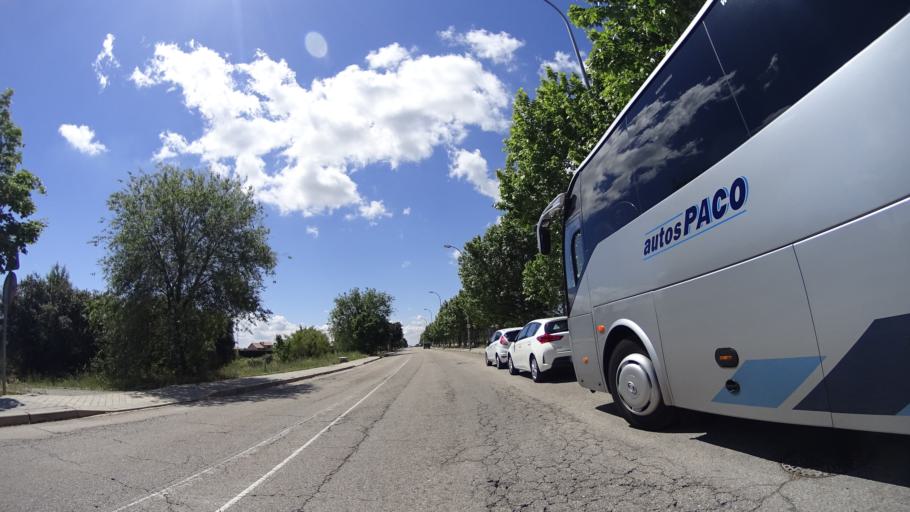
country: ES
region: Madrid
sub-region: Provincia de Madrid
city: Colmenarejo
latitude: 40.5517
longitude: -4.0116
